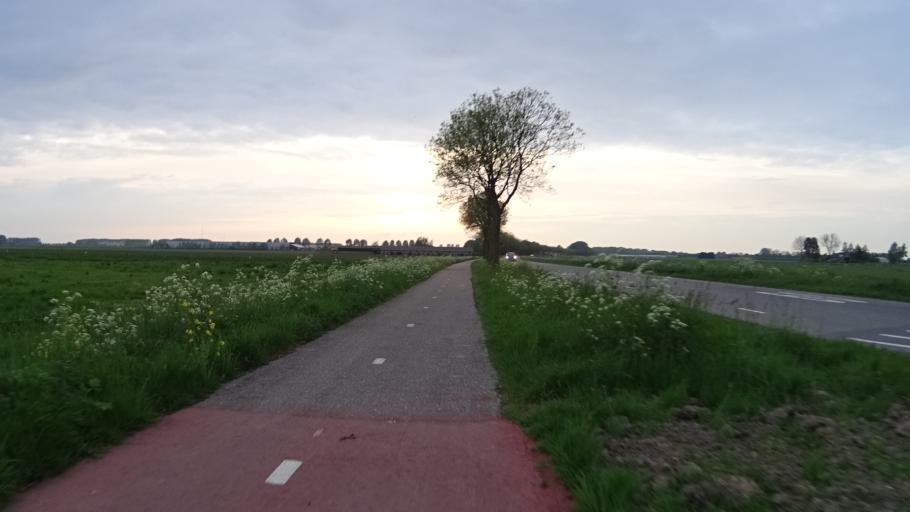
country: NL
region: North Brabant
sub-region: Gemeente Woudrichem
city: Woudrichem
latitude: 51.7776
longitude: 5.0511
